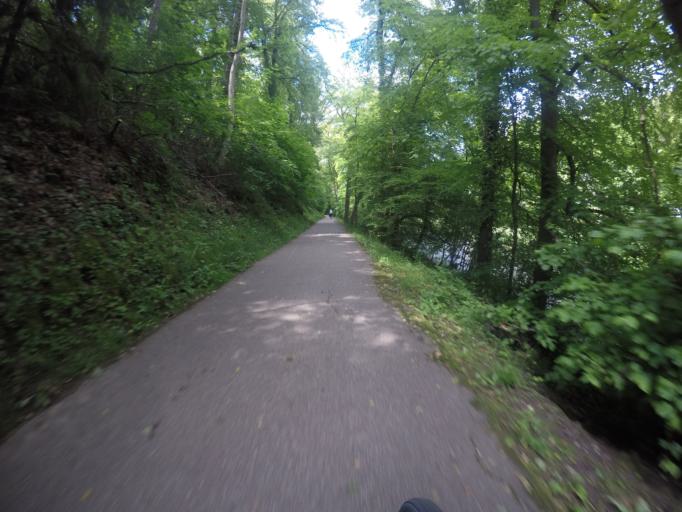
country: DE
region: Baden-Wuerttemberg
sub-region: Karlsruhe Region
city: Pforzheim
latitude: 48.8726
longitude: 8.6764
